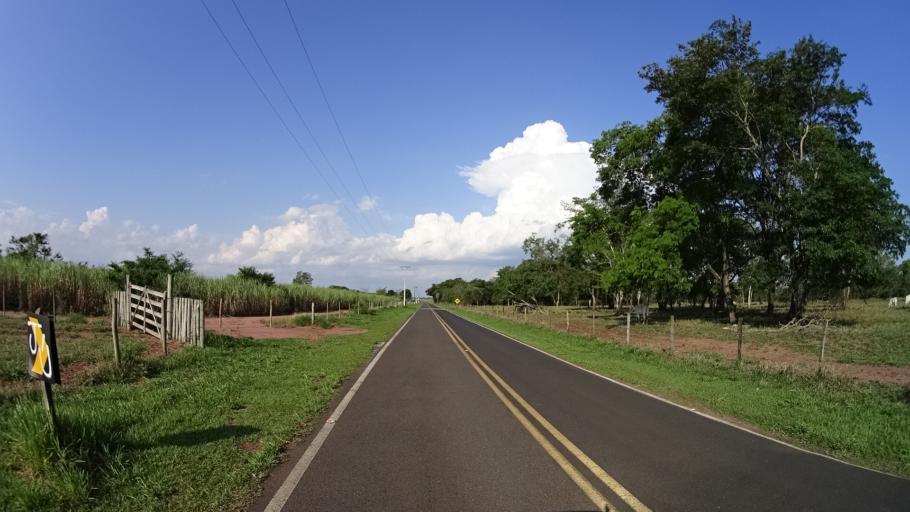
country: BR
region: Sao Paulo
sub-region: Urupes
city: Urupes
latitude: -21.3962
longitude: -49.5131
